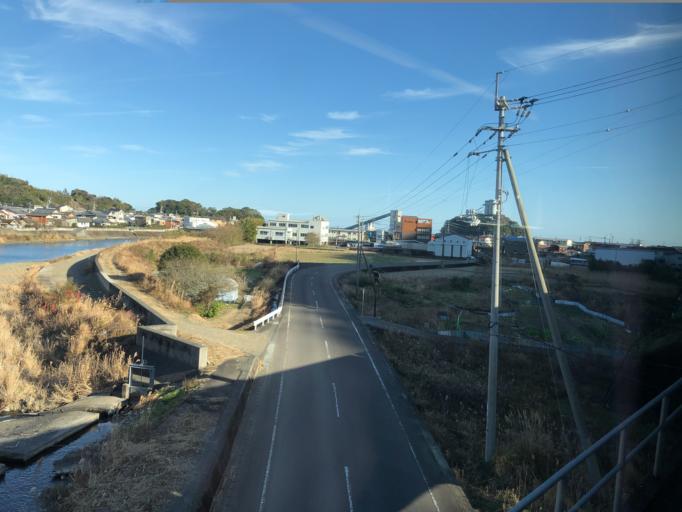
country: JP
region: Kochi
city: Nakamura
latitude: 33.0788
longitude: 133.1022
